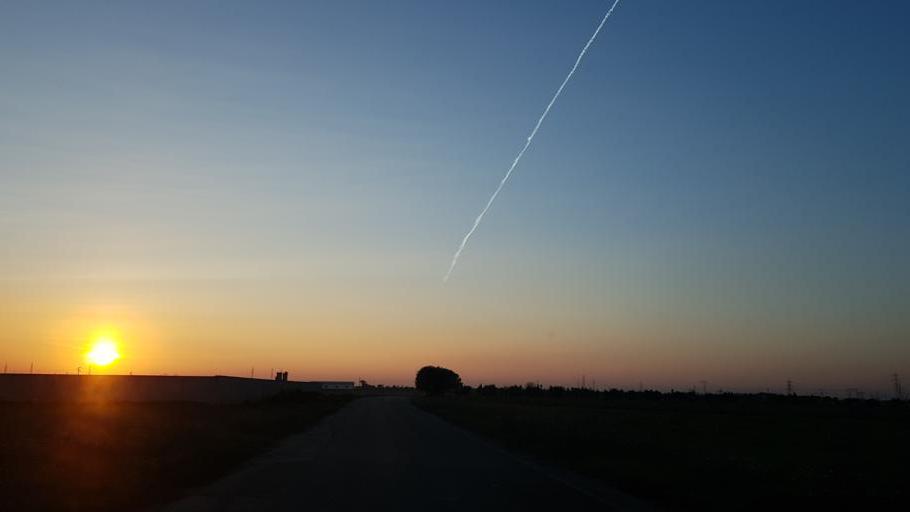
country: IT
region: Apulia
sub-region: Provincia di Brindisi
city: La Rosa
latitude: 40.5901
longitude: 17.9273
